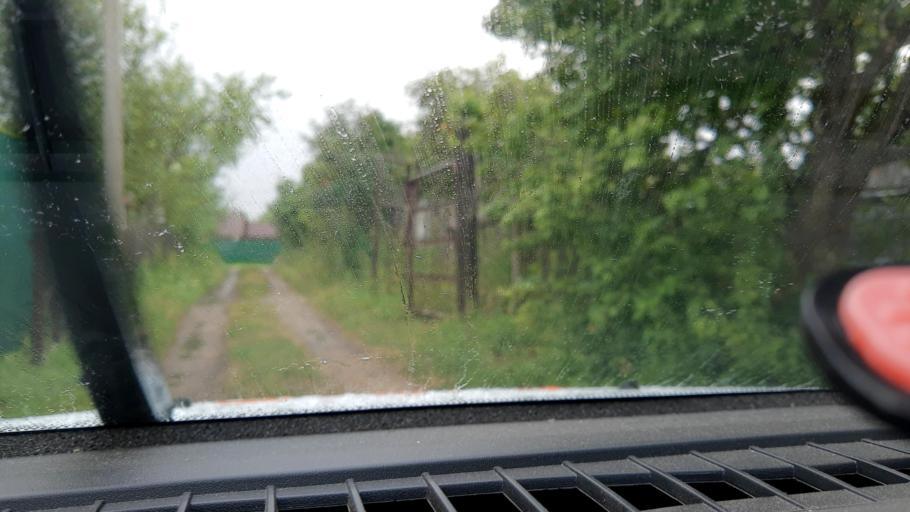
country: RU
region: Nizjnij Novgorod
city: Zavolzh'ye
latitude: 56.6604
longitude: 43.4224
